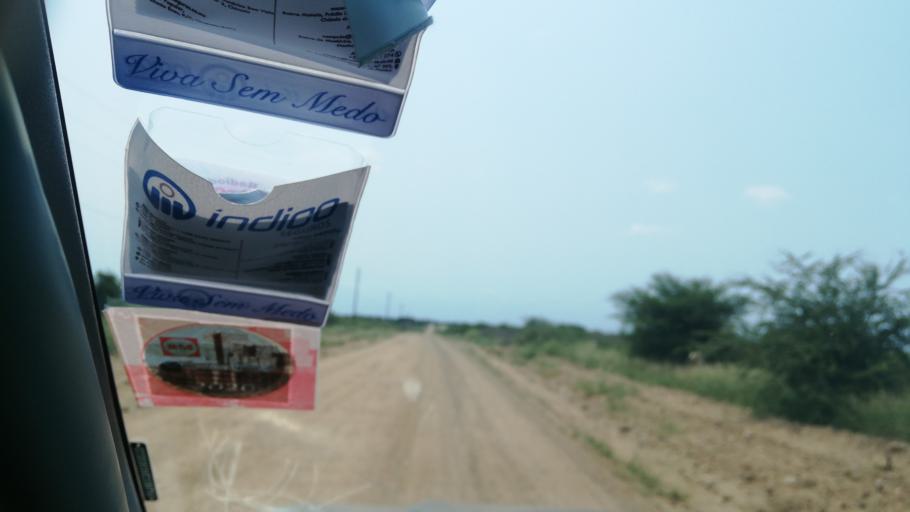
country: MZ
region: Maputo
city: Matola
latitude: -26.0723
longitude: 32.3907
